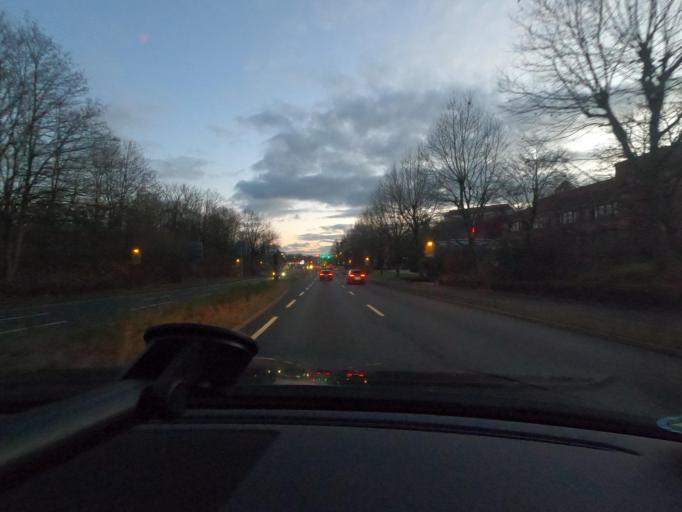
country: DE
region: Lower Saxony
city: Herzberg am Harz
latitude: 51.6592
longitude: 10.3335
